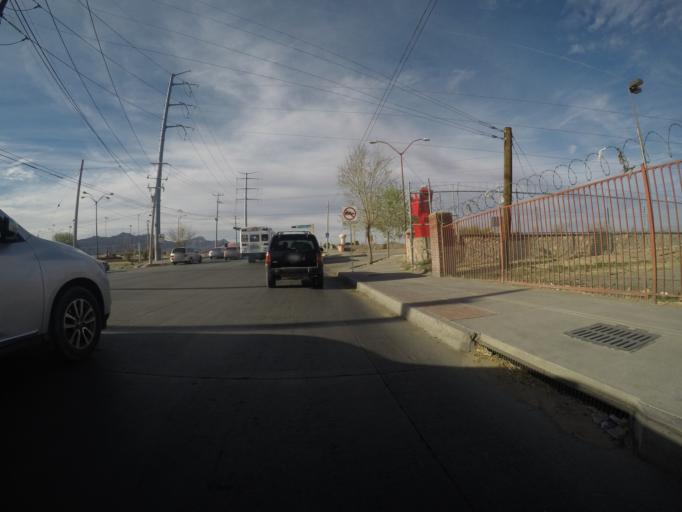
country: US
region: Texas
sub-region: El Paso County
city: El Paso
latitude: 31.7537
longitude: -106.4413
